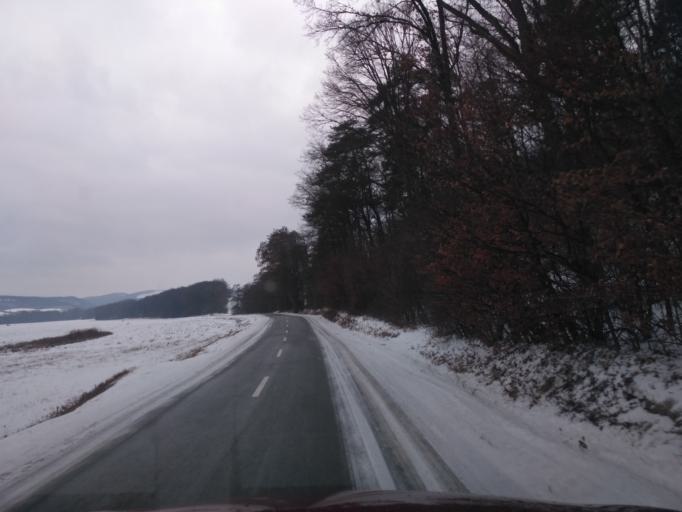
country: SK
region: Presovsky
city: Sabinov
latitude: 49.0495
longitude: 21.0937
